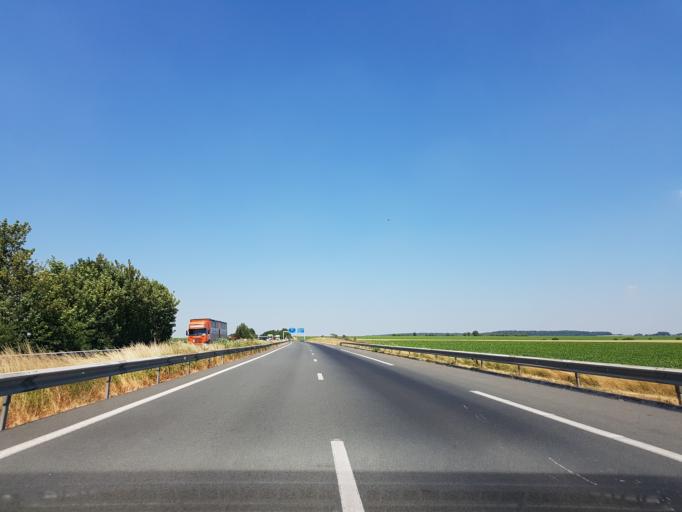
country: FR
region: Nord-Pas-de-Calais
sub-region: Departement du Nord
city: Marcoing
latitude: 50.1301
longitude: 3.1480
